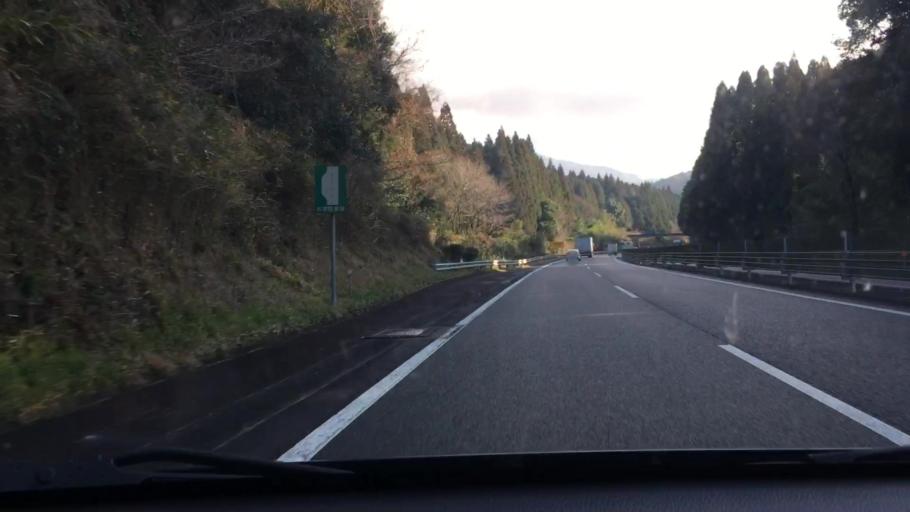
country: JP
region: Kagoshima
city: Okuchi-shinohara
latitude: 32.0010
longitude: 130.7577
